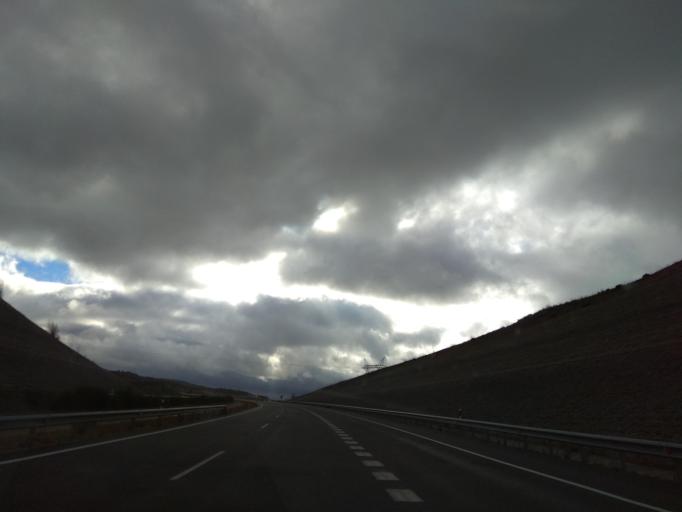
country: ES
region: Castille and Leon
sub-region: Provincia de Burgos
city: Sotragero
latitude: 42.3930
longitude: -3.6976
